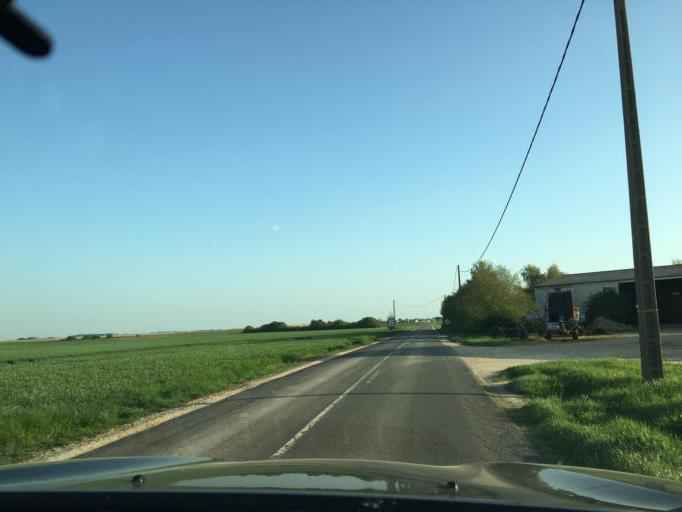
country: FR
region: Centre
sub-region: Departement du Loir-et-Cher
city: Ouzouer-le-Marche
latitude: 47.8804
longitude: 1.5325
